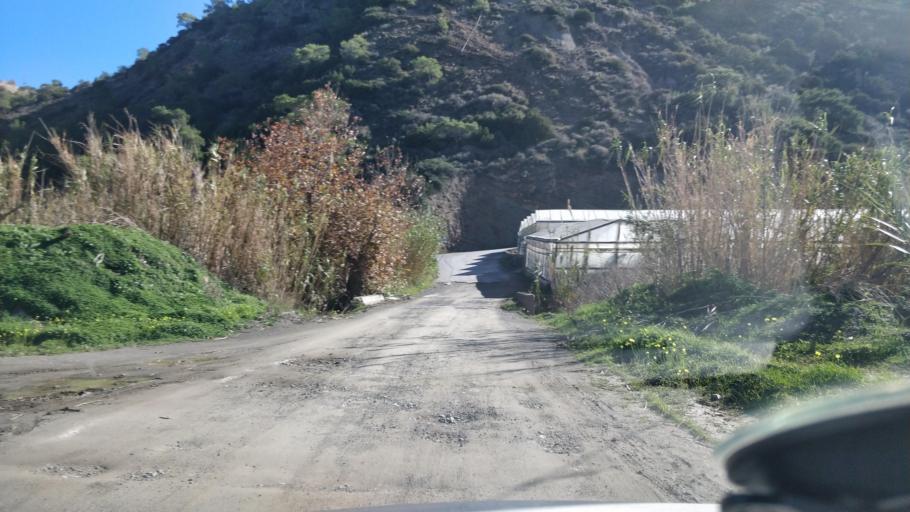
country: GR
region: Crete
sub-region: Nomos Lasithiou
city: Gra Liyia
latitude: 34.9904
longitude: 25.4839
